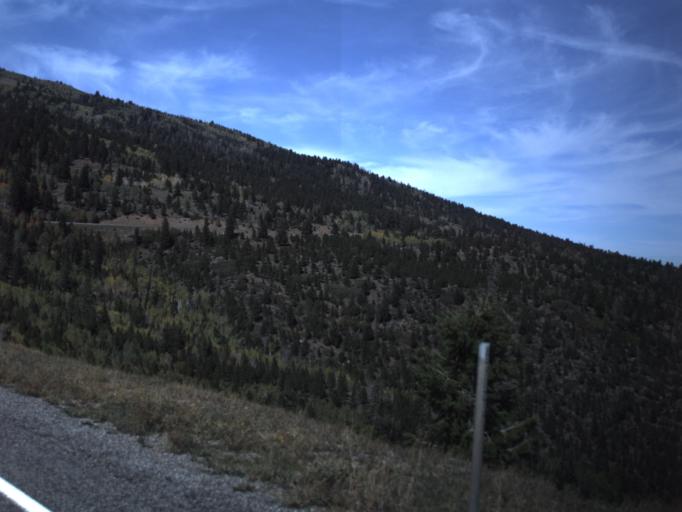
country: US
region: Utah
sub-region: Wayne County
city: Loa
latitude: 38.1204
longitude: -111.3268
